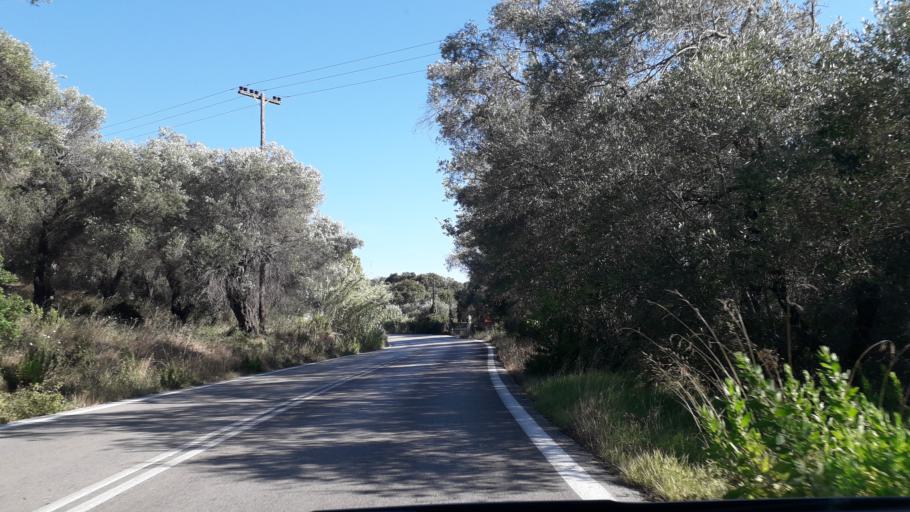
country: GR
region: Ionian Islands
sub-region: Nomos Kerkyras
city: Agios Matthaios
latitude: 39.4502
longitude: 19.9279
